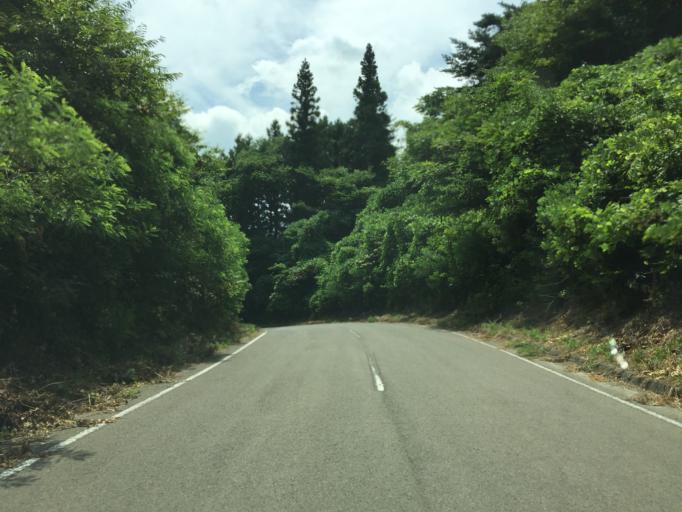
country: JP
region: Fukushima
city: Hobaramachi
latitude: 37.6554
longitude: 140.6506
